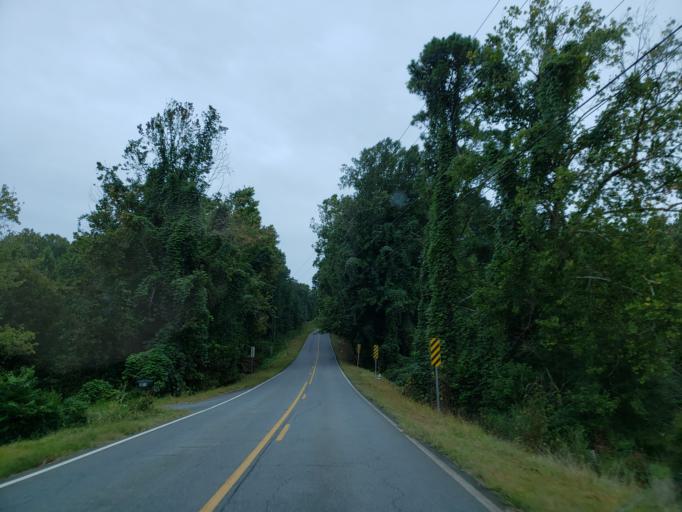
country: US
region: Georgia
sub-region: Cherokee County
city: Ball Ground
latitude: 34.3577
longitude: -84.4869
